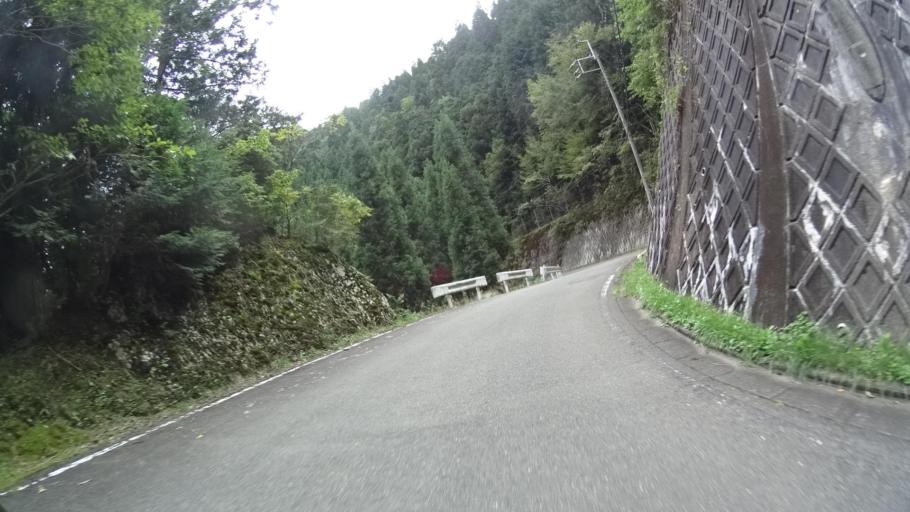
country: JP
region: Shiga Prefecture
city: Kitahama
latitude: 35.2378
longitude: 135.7804
